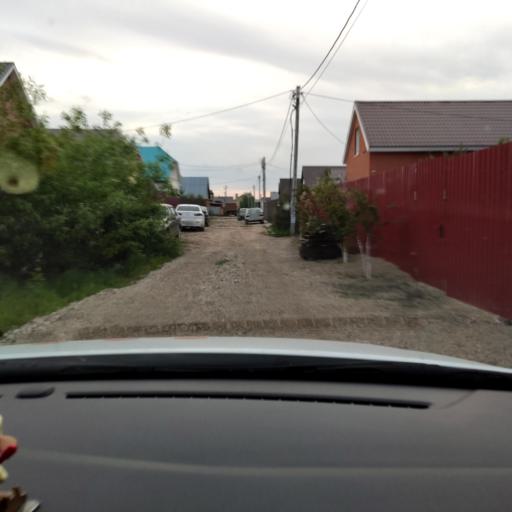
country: RU
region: Tatarstan
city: Stolbishchi
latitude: 55.7453
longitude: 49.2924
